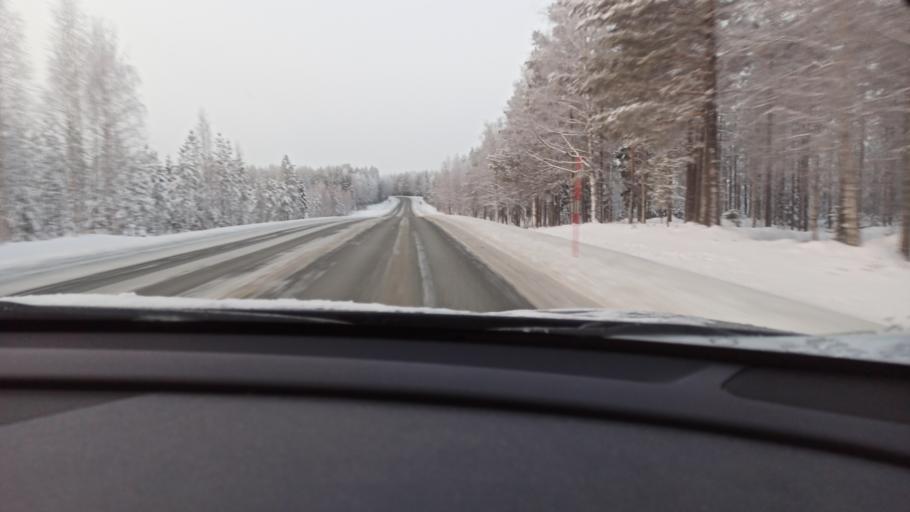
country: FI
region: Lapland
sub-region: Rovaniemi
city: Rovaniemi
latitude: 66.5617
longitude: 25.9233
